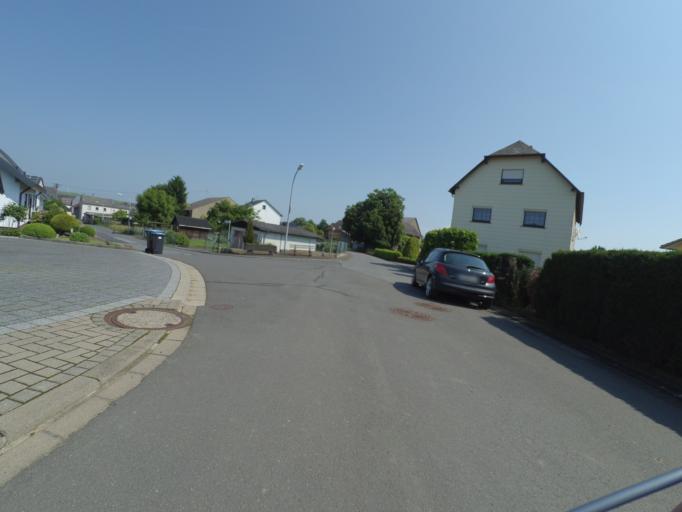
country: DE
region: Rheinland-Pfalz
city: Kollig
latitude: 50.2626
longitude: 7.2776
